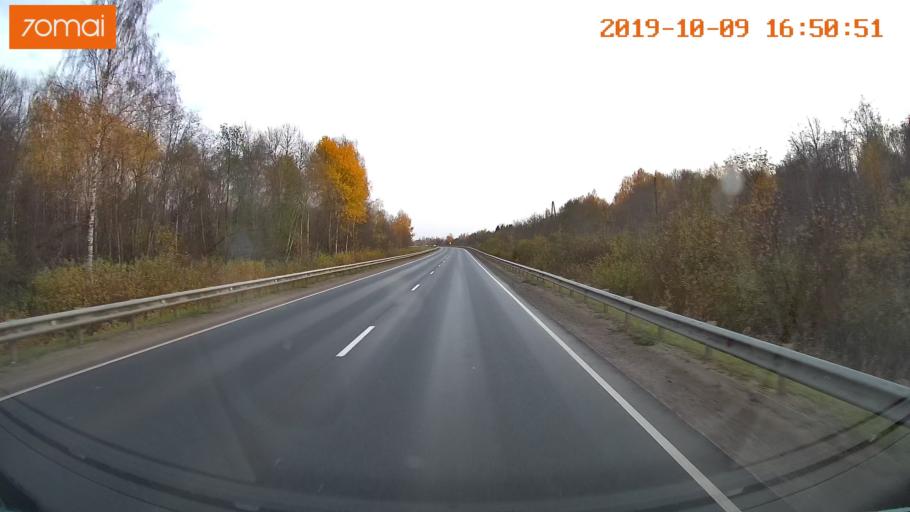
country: RU
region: Ivanovo
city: Privolzhsk
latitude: 57.3952
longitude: 41.2142
